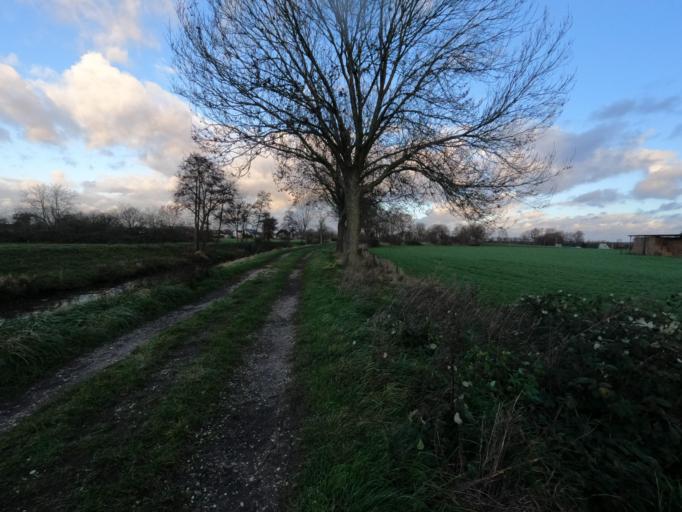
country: DE
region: North Rhine-Westphalia
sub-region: Regierungsbezirk Koln
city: Heinsberg
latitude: 51.0915
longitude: 6.1132
